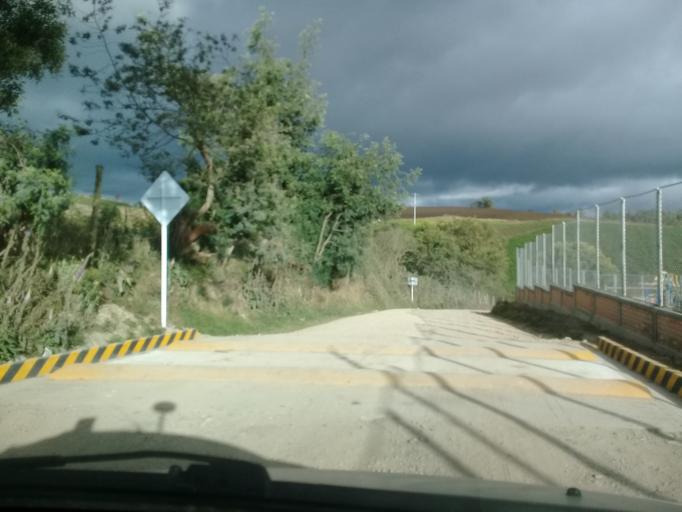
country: CO
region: Cundinamarca
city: Villapinzon
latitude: 5.2389
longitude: -73.6511
